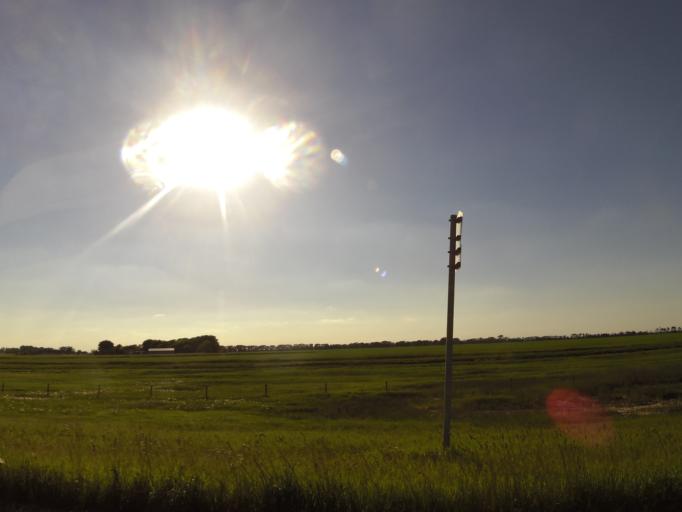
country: US
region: North Dakota
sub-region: Grand Forks County
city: Grand Forks
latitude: 48.1363
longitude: -97.1924
